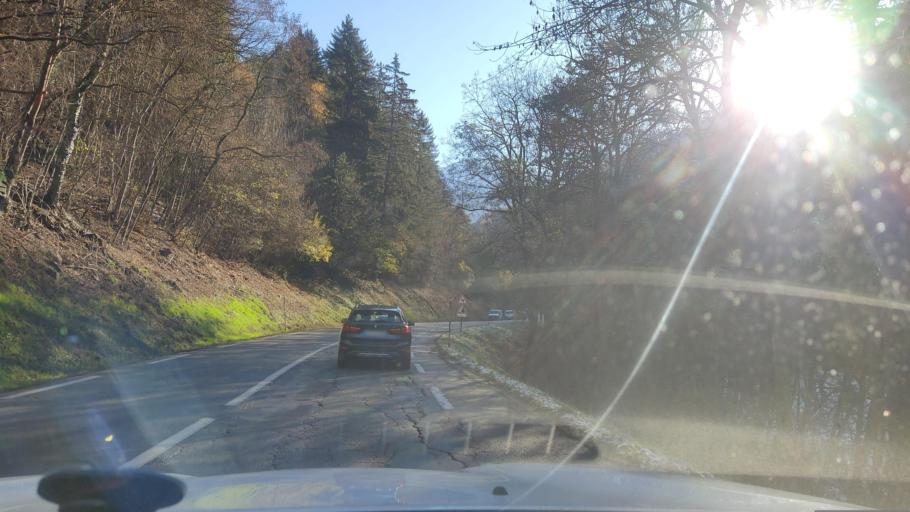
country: FR
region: Rhone-Alpes
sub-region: Departement de la Savoie
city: Seez
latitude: 45.6110
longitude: 6.8348
